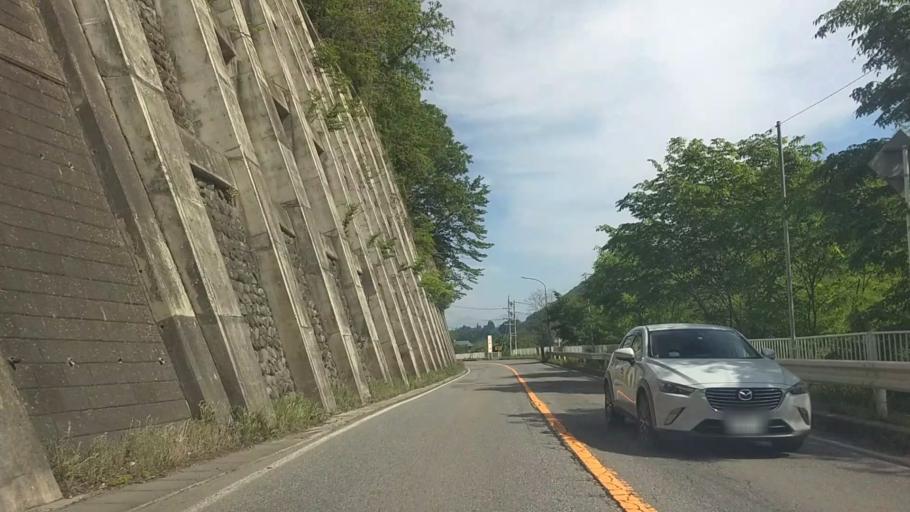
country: JP
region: Nagano
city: Saku
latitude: 36.1070
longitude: 138.4789
